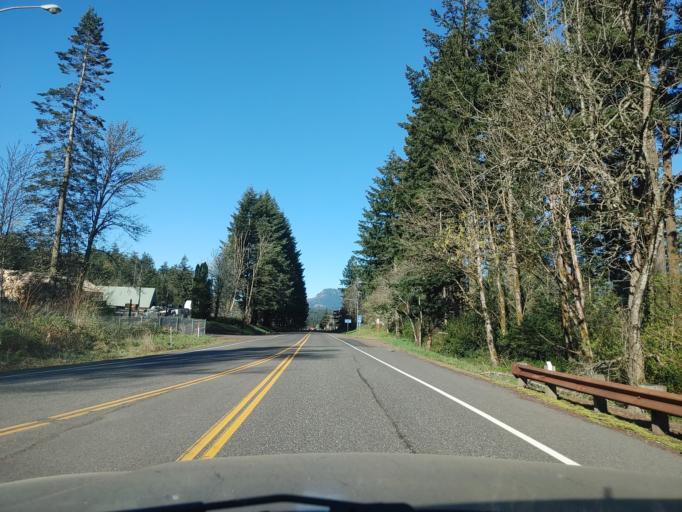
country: US
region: Oregon
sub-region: Hood River County
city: Cascade Locks
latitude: 45.6729
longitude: -121.8781
